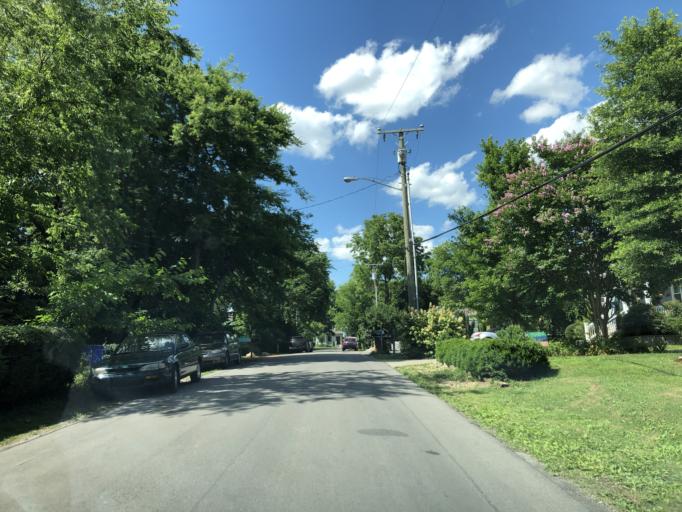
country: US
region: Tennessee
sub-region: Davidson County
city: Nashville
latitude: 36.1795
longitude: -86.7349
